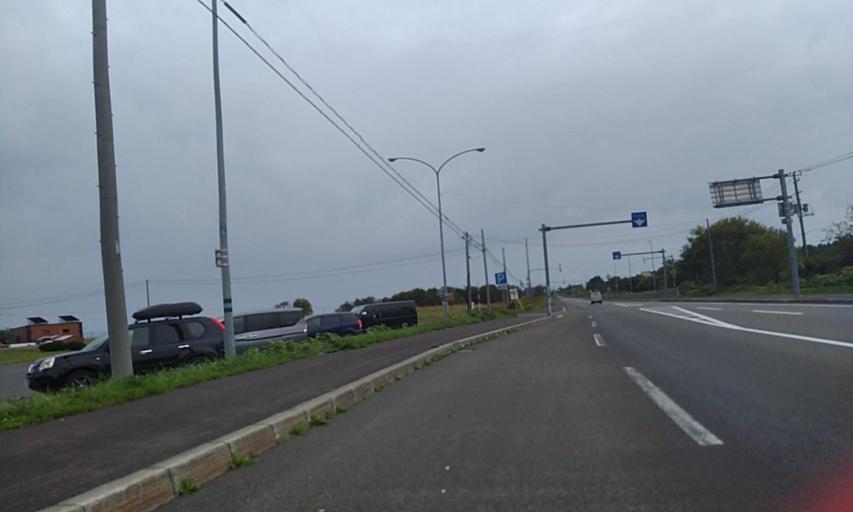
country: JP
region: Hokkaido
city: Nayoro
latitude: 44.8780
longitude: 142.6306
